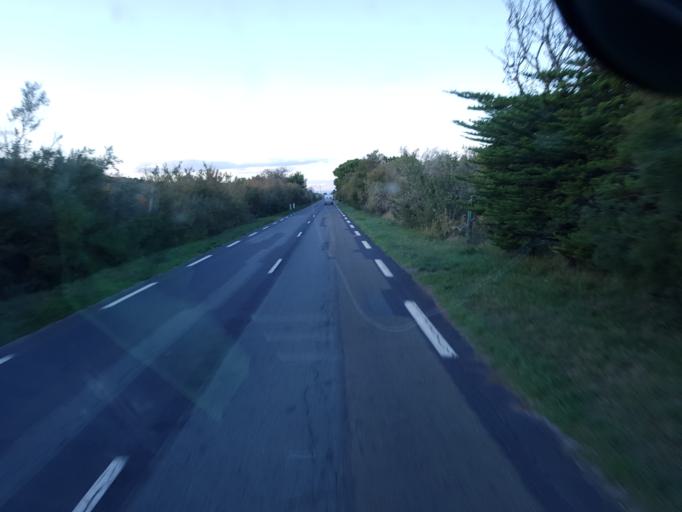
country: FR
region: Languedoc-Roussillon
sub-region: Departement de l'Aude
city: Port-la-Nouvelle
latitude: 43.0047
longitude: 3.0395
